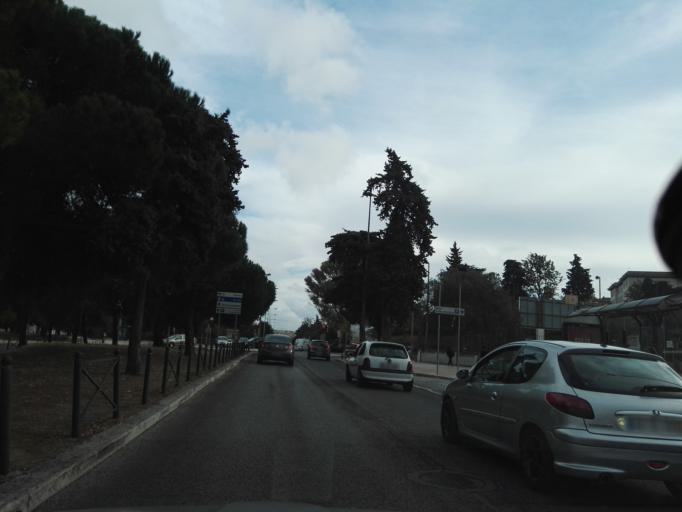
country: PT
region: Lisbon
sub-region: Odivelas
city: Olival do Basto
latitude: 38.7508
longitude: -9.1588
